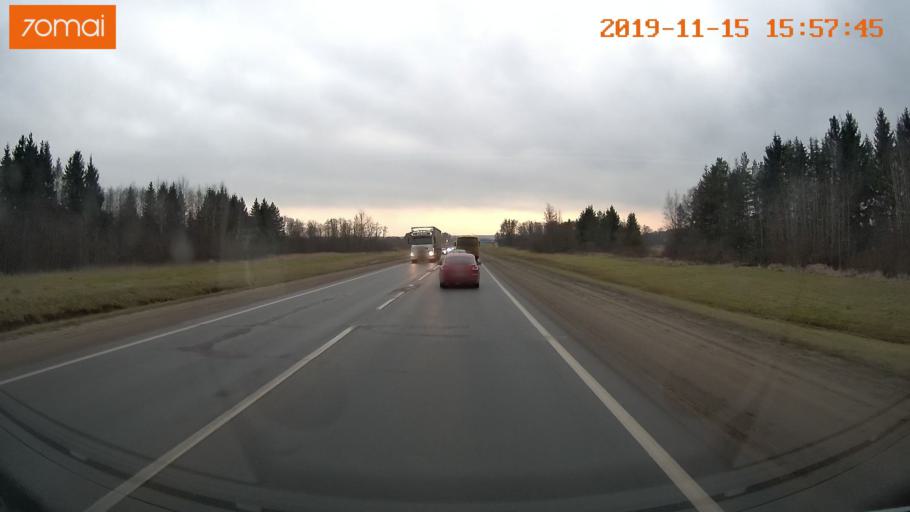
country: RU
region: Jaroslavl
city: Yaroslavl
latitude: 57.8270
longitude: 39.9607
